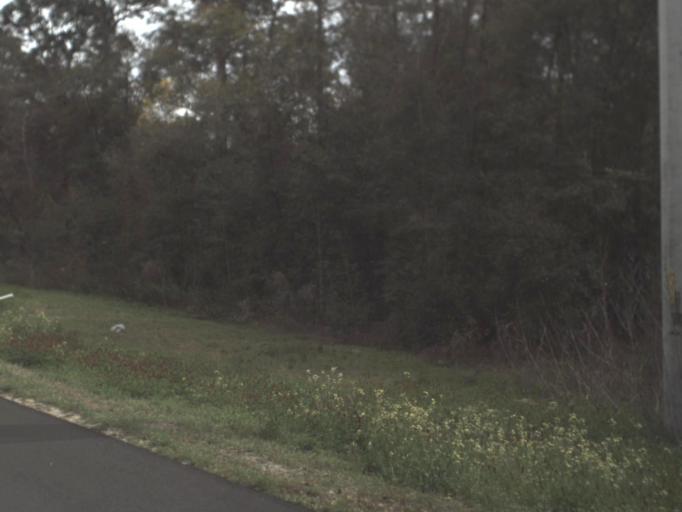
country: US
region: Florida
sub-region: Gadsden County
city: Midway
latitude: 30.4420
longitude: -84.3904
